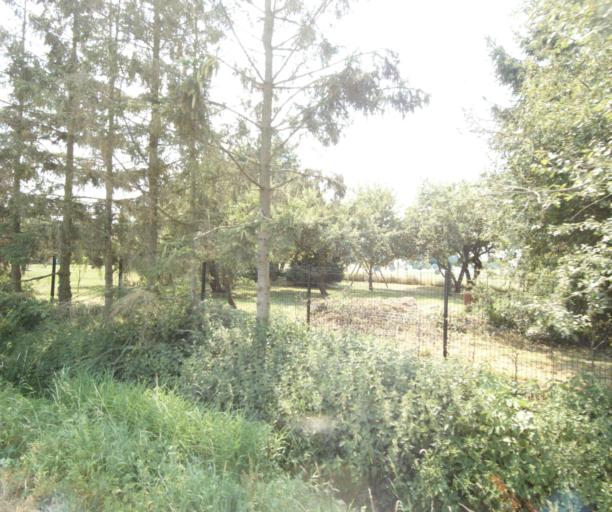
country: FR
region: Nord-Pas-de-Calais
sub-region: Departement du Nord
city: Wambrechies
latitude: 50.7135
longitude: 3.0418
